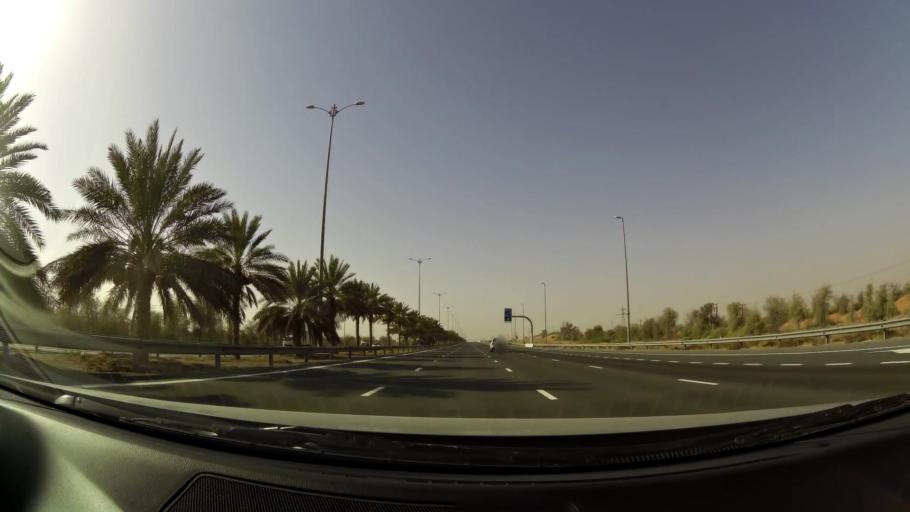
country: OM
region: Al Buraimi
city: Al Buraymi
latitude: 24.5245
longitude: 55.7613
